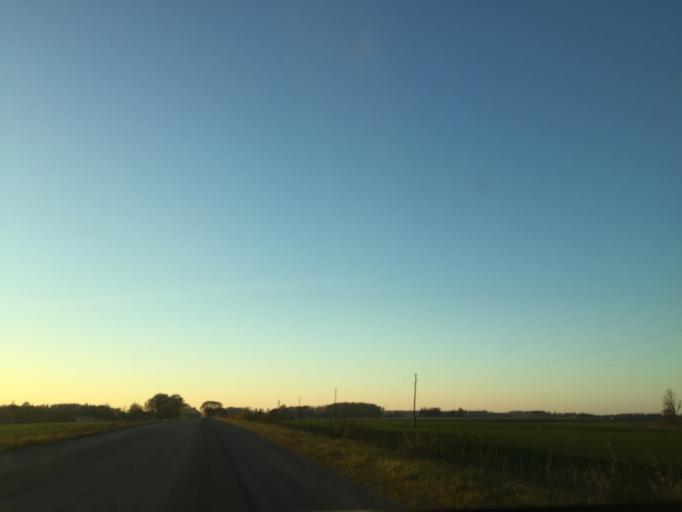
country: LT
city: Vieksniai
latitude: 56.4016
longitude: 22.5348
